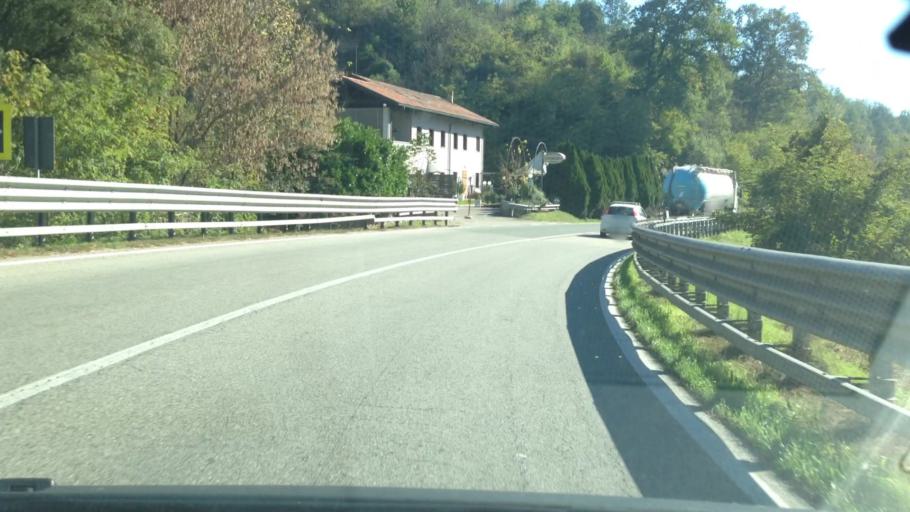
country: IT
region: Piedmont
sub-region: Provincia di Asti
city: Castello di Annone
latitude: 44.8902
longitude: 8.3070
